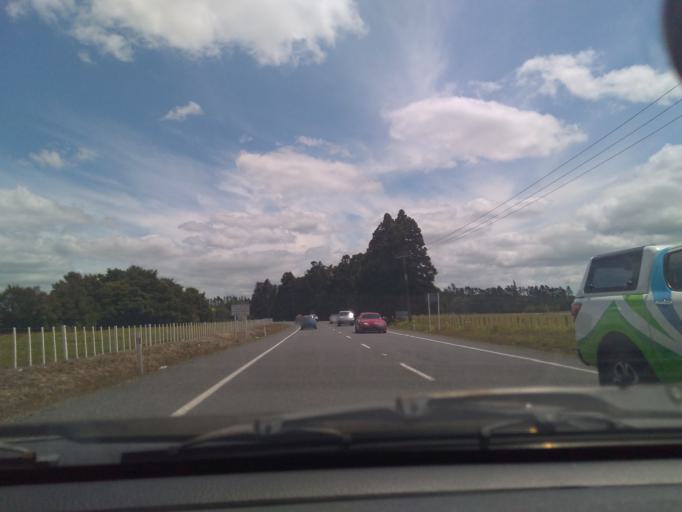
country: NZ
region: Northland
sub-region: Far North District
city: Kerikeri
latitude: -35.2299
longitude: 173.9184
